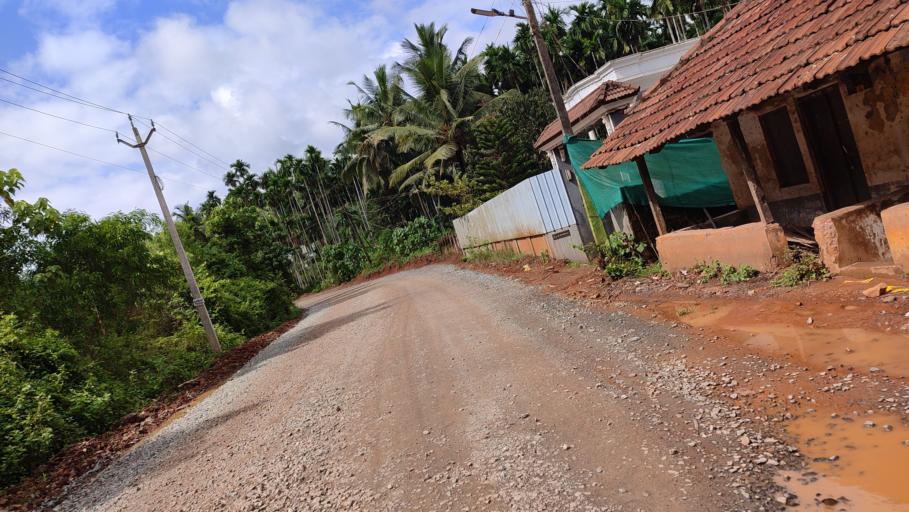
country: IN
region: Kerala
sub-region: Kasaragod District
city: Kasaragod
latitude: 12.5179
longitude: 75.0718
